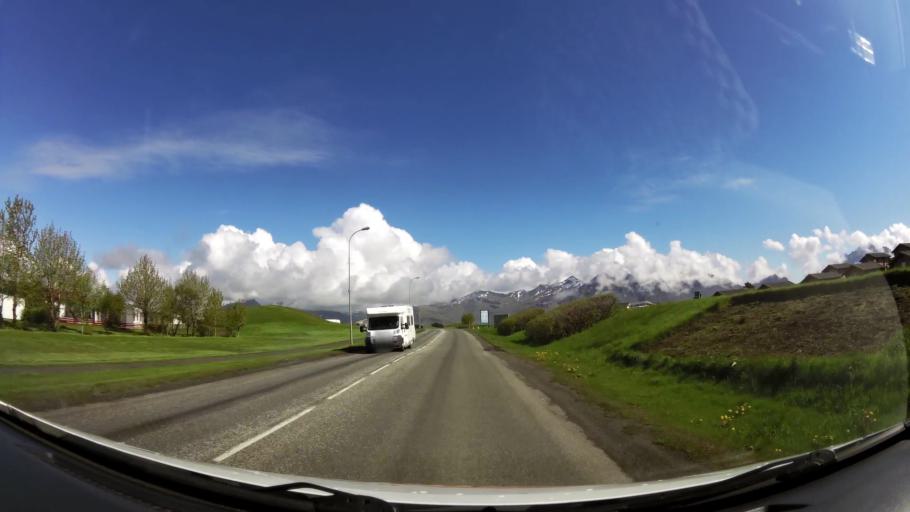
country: IS
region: East
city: Hoefn
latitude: 64.2574
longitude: -15.2058
